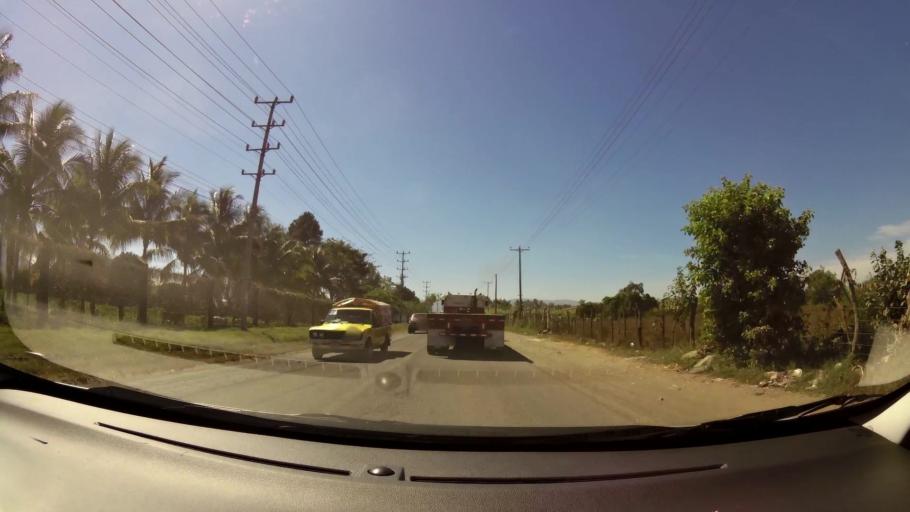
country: SV
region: La Libertad
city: San Juan Opico
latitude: 13.7976
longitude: -89.3658
